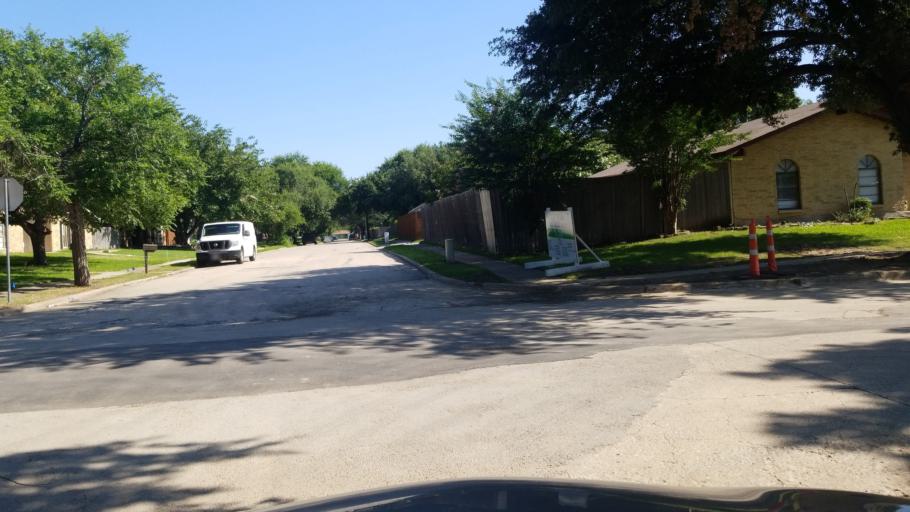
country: US
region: Texas
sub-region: Dallas County
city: Grand Prairie
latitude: 32.6834
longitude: -97.0125
